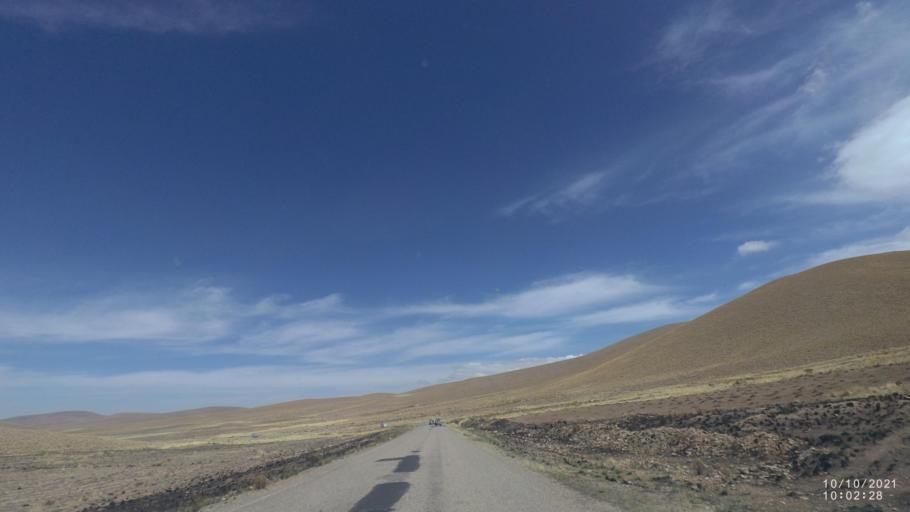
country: BO
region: La Paz
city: Eucaliptus
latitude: -17.3602
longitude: -67.4335
